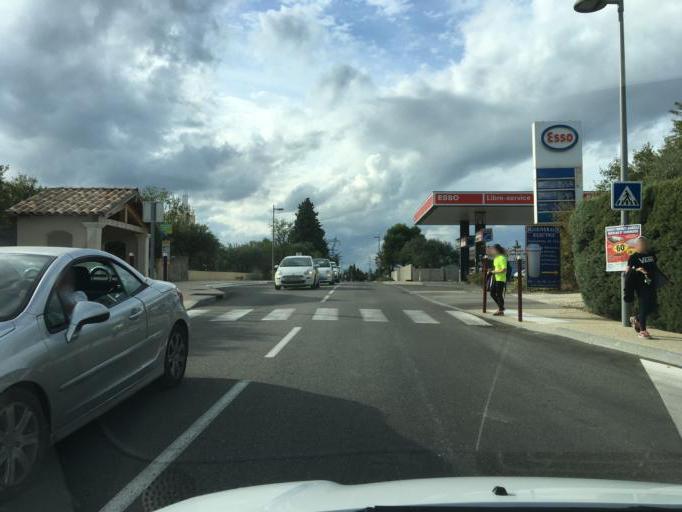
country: FR
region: Provence-Alpes-Cote d'Azur
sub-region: Departement du Vaucluse
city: Chateauneuf-de-Gadagne
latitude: 43.9285
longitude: 4.9384
